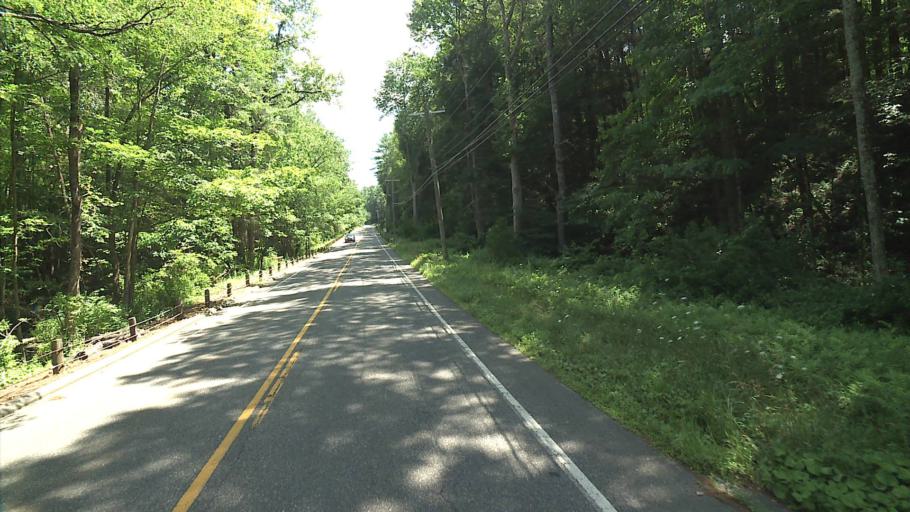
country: US
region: Connecticut
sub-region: Litchfield County
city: Canaan
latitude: 41.8742
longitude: -73.3386
